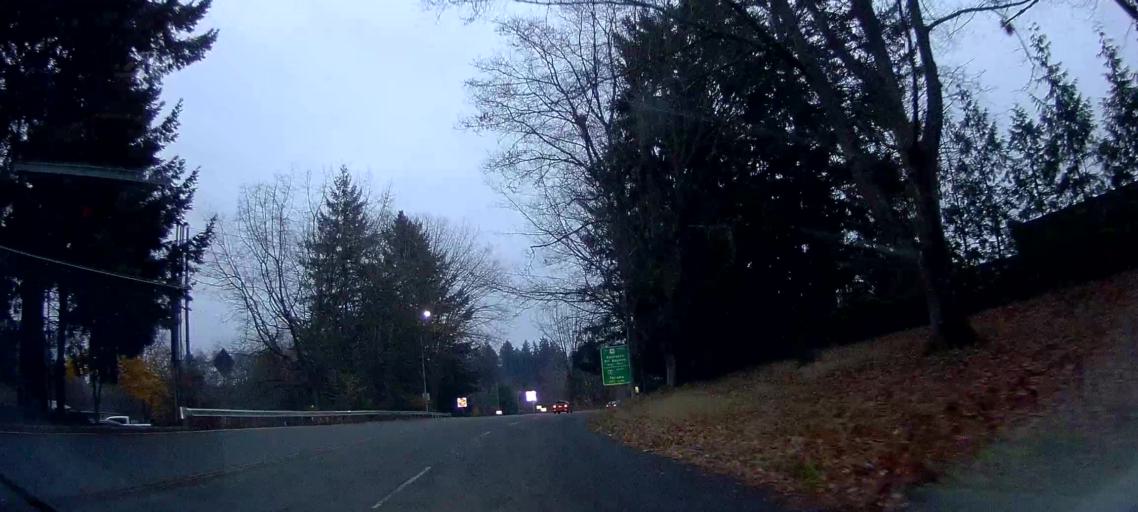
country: US
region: Washington
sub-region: Thurston County
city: Olympia
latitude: 47.0352
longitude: -122.8937
